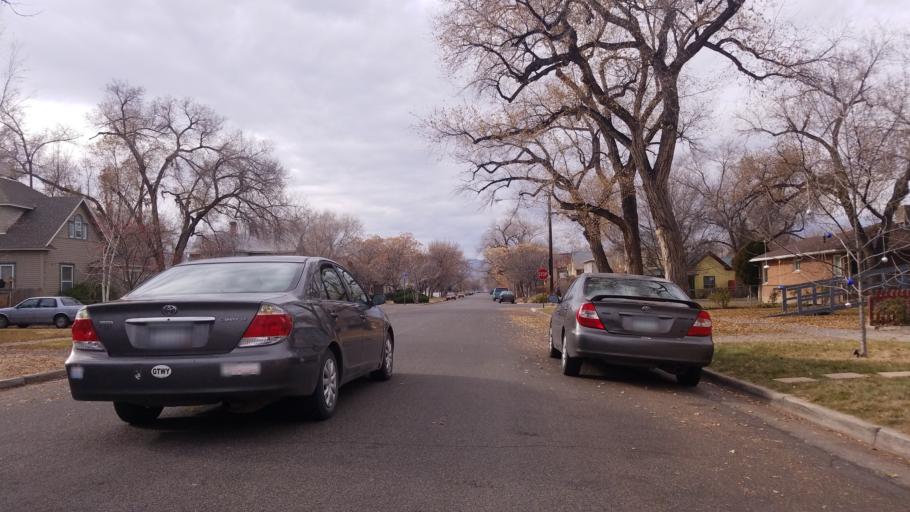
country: US
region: Colorado
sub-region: Mesa County
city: Grand Junction
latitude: 39.0693
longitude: -108.5553
